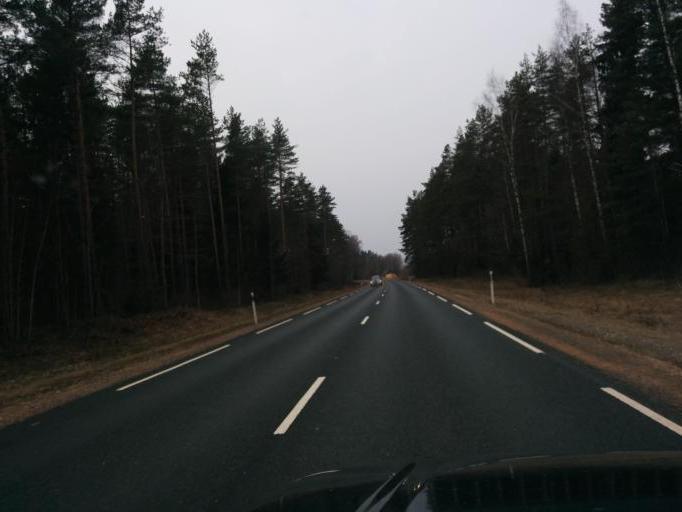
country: LV
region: Ogre
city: Ogre
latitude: 56.8044
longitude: 24.5726
